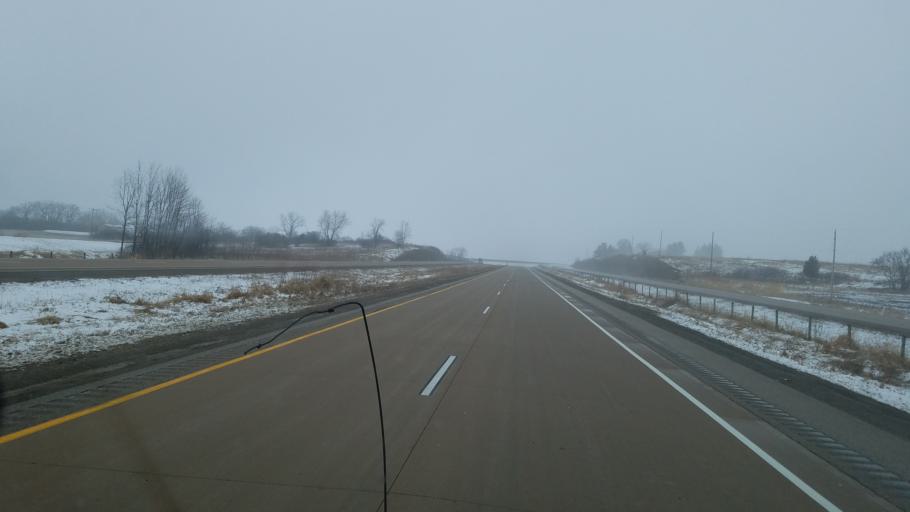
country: US
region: Wisconsin
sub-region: Winnebago County
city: Winneconne
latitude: 44.1485
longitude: -88.6641
